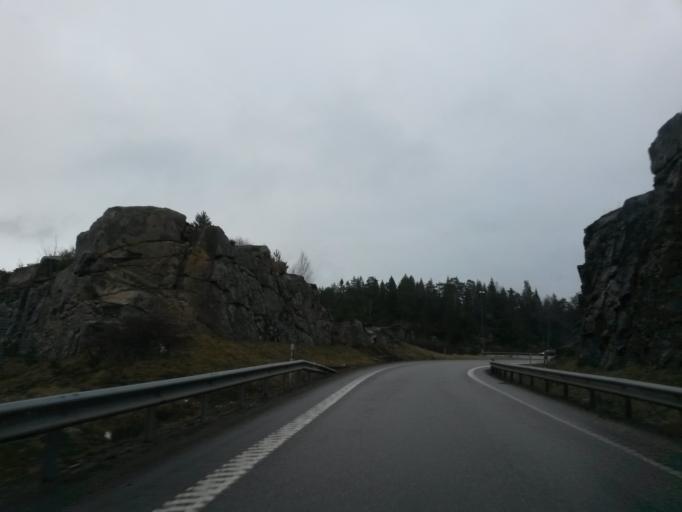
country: SE
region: Vaestra Goetaland
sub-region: Uddevalla Kommun
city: Uddevalla
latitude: 58.3354
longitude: 11.9895
